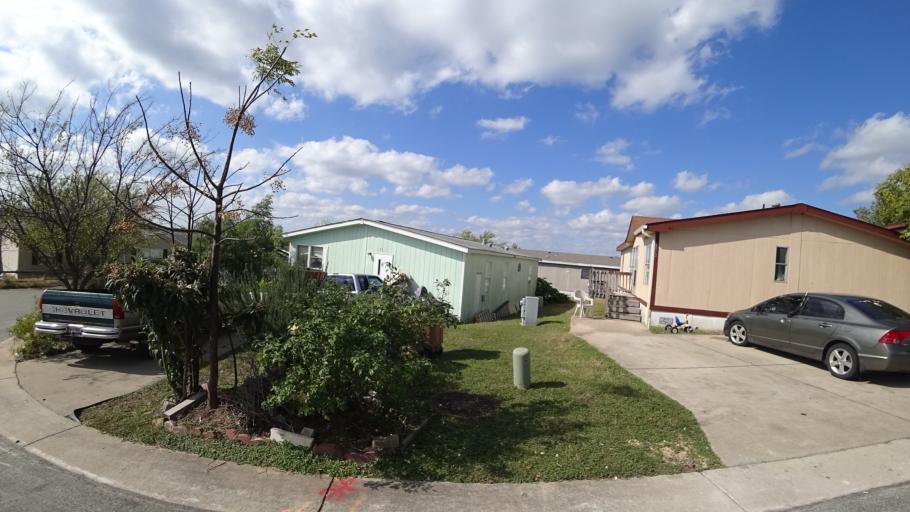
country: US
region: Texas
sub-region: Travis County
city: Barton Creek
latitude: 30.2498
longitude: -97.8819
